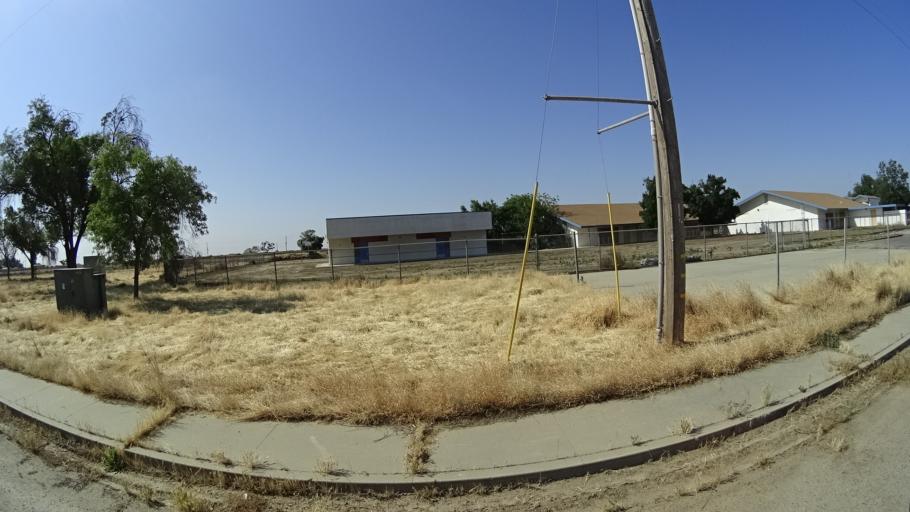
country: US
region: California
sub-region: Kings County
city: Home Garden
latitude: 36.3018
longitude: -119.6293
